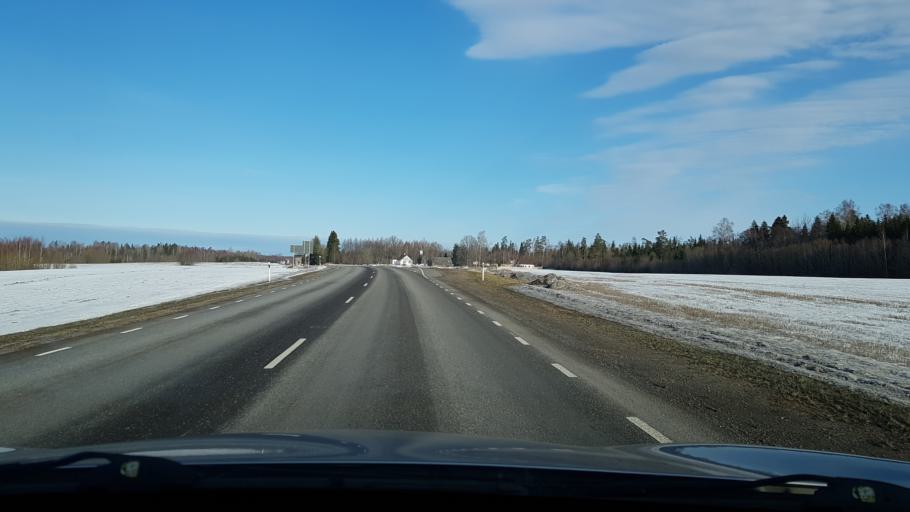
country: EE
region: Viljandimaa
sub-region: Viljandi linn
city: Viljandi
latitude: 58.4235
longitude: 25.5984
